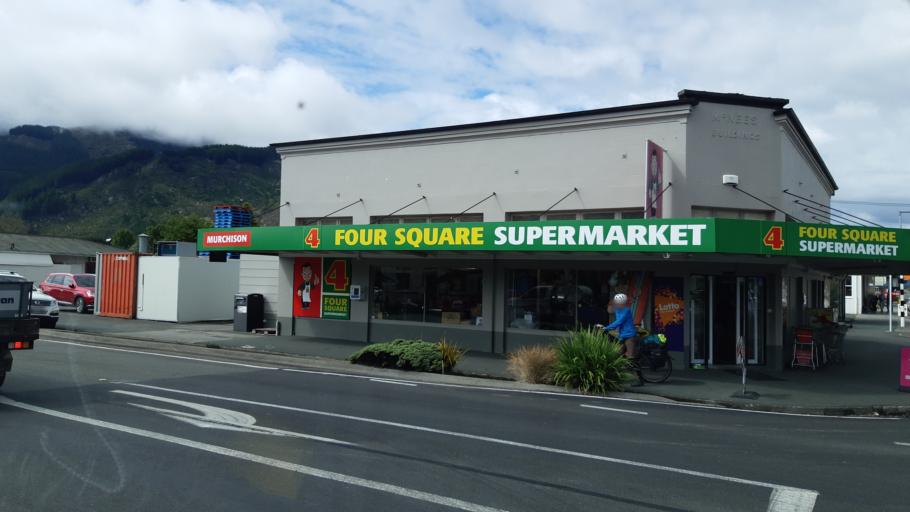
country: NZ
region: West Coast
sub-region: Buller District
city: Westport
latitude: -41.8000
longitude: 172.3255
